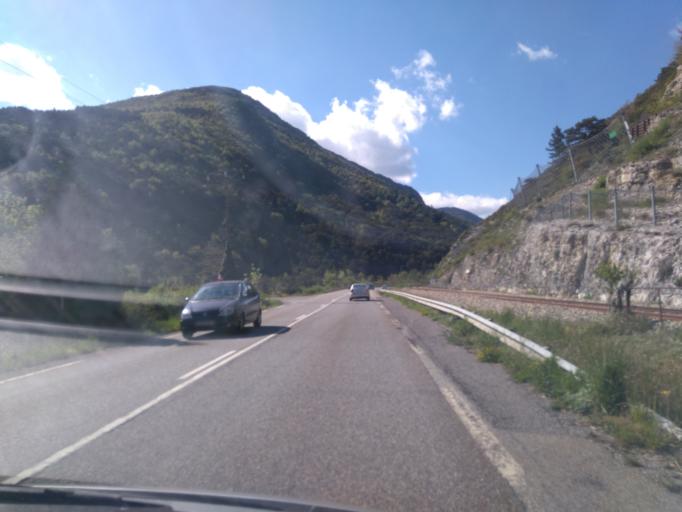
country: FR
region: Provence-Alpes-Cote d'Azur
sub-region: Departement des Hautes-Alpes
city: Veynes
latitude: 44.5765
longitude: 5.7268
